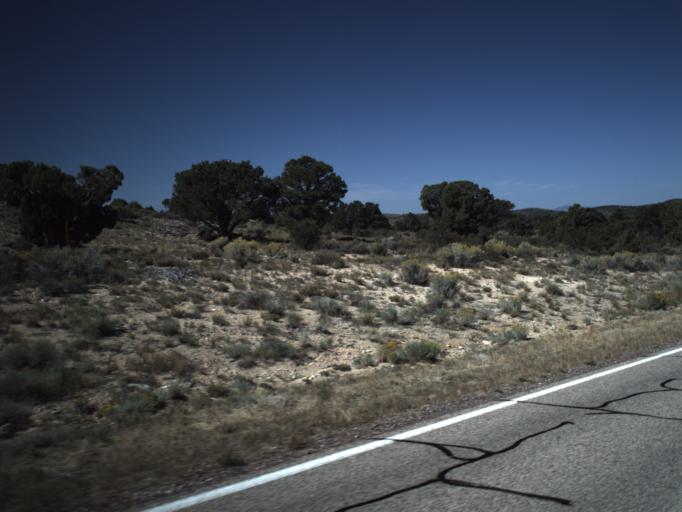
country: US
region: Utah
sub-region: Washington County
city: Enterprise
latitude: 37.6448
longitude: -113.4428
